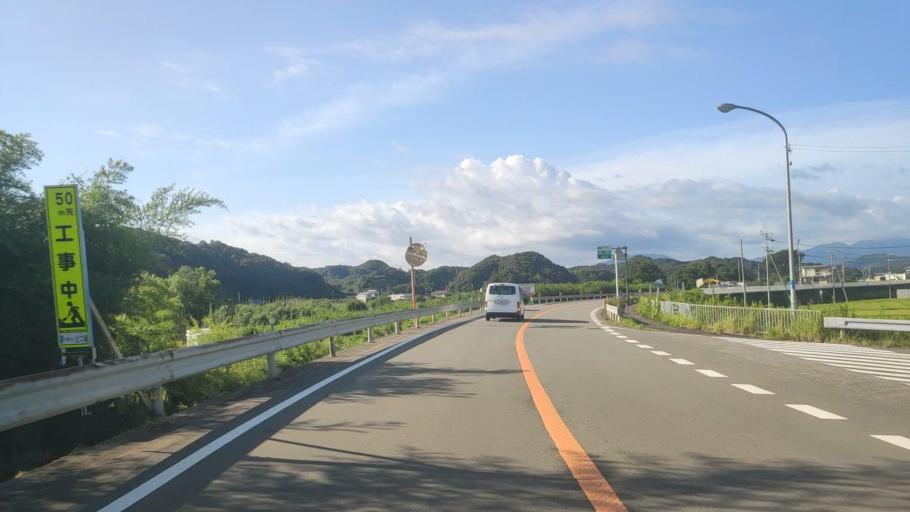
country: JP
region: Wakayama
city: Tanabe
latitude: 33.6763
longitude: 135.4076
